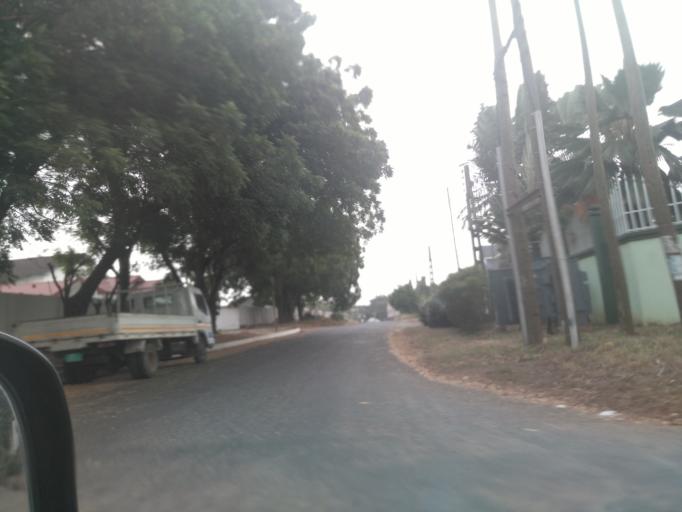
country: GH
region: Greater Accra
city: Accra
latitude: 5.6042
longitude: -0.1869
